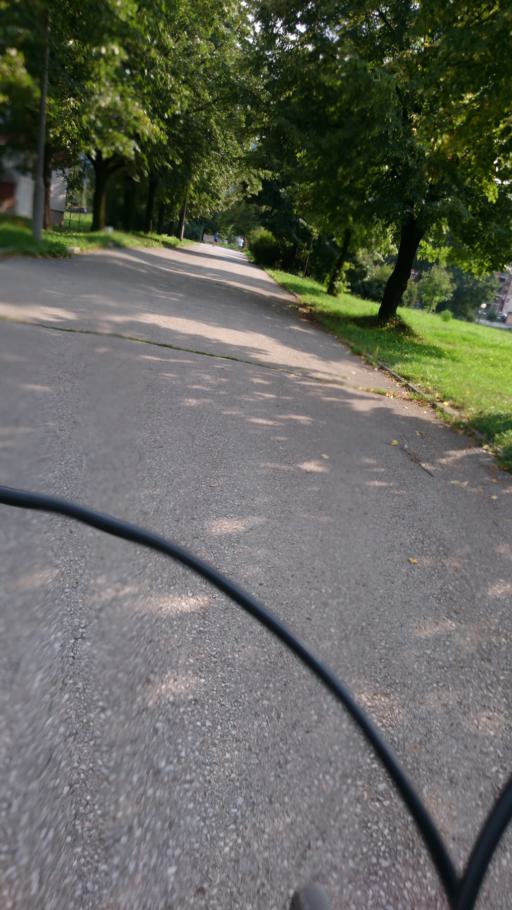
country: BA
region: Federation of Bosnia and Herzegovina
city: Zenica
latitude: 44.2009
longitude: 17.9238
